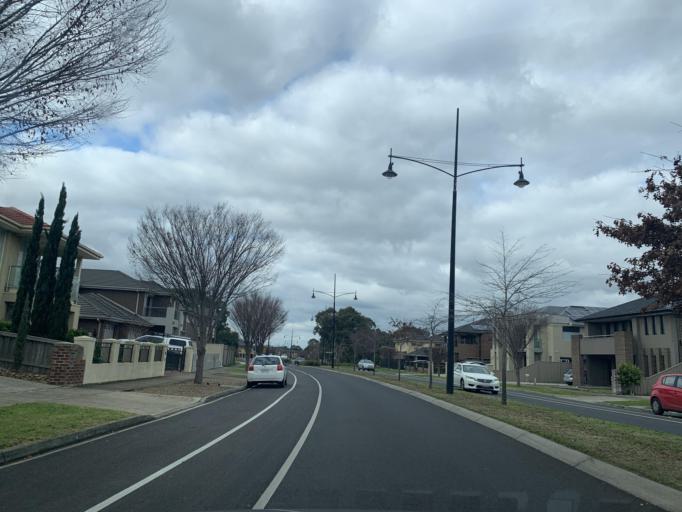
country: AU
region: Victoria
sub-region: Whittlesea
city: Epping
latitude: -37.6304
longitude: 145.0168
